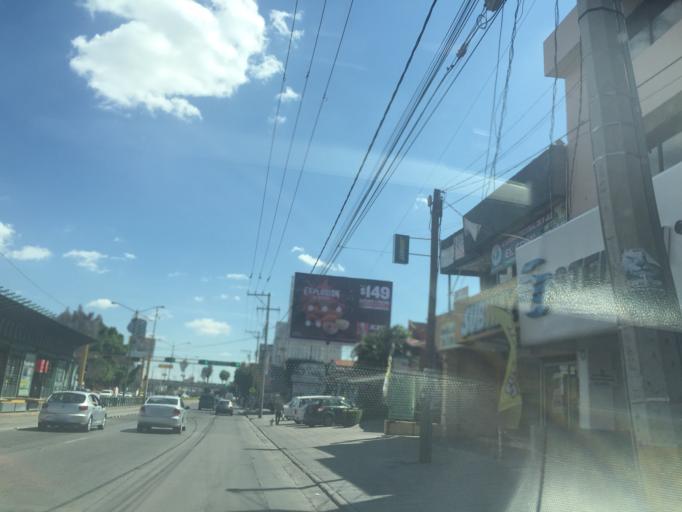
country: MX
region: Guanajuato
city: Leon
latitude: 21.1434
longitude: -101.6860
